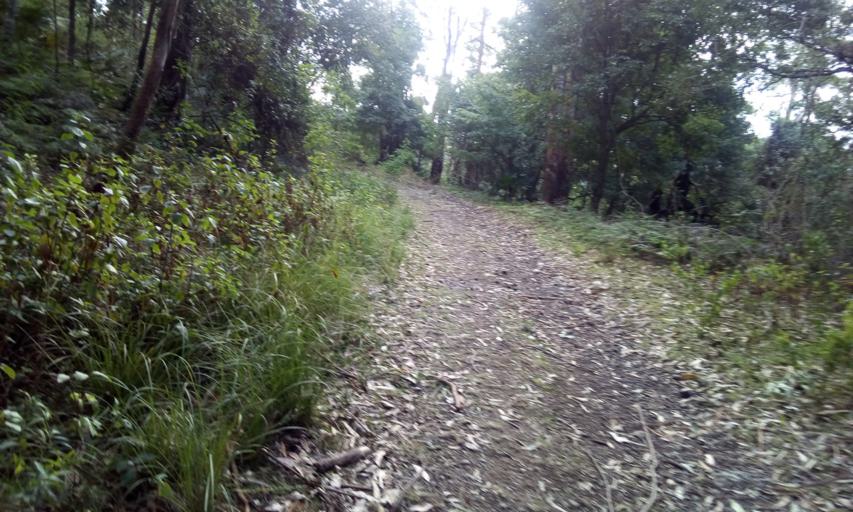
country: AU
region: New South Wales
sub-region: Wollongong
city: Cordeaux Heights
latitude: -34.4391
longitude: 150.8133
